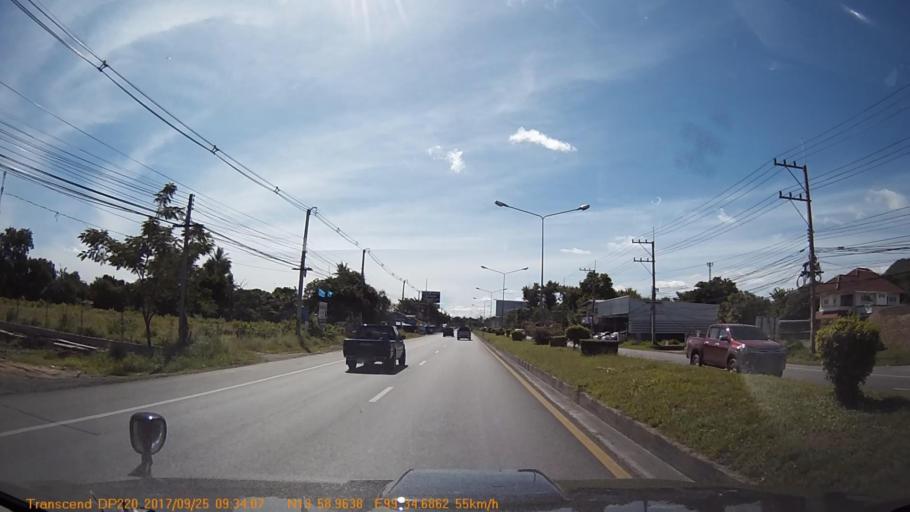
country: TH
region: Kanchanaburi
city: Kanchanaburi
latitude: 13.9826
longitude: 99.5783
